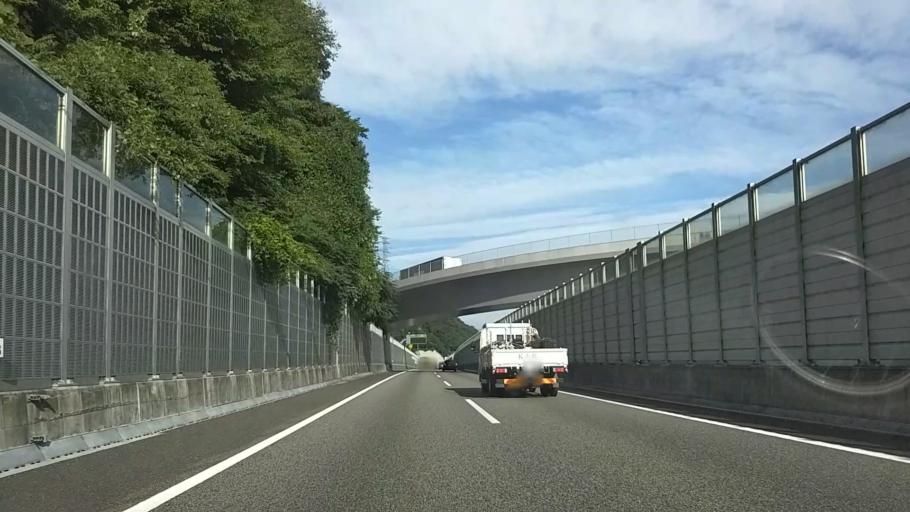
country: JP
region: Kanagawa
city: Zama
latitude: 35.5227
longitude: 139.3545
